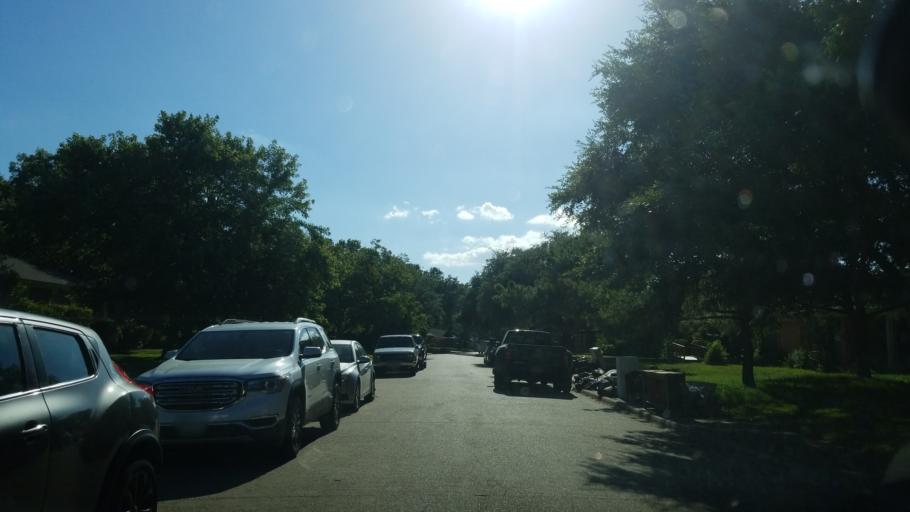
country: US
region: Texas
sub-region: Dallas County
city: Balch Springs
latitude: 32.7872
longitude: -96.7021
